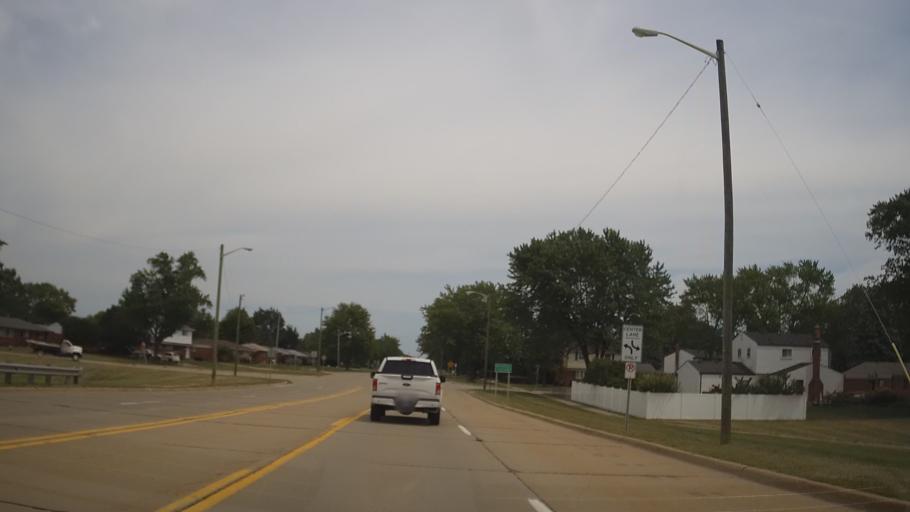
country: US
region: Michigan
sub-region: Macomb County
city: Sterling Heights
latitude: 42.5806
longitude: -83.0227
